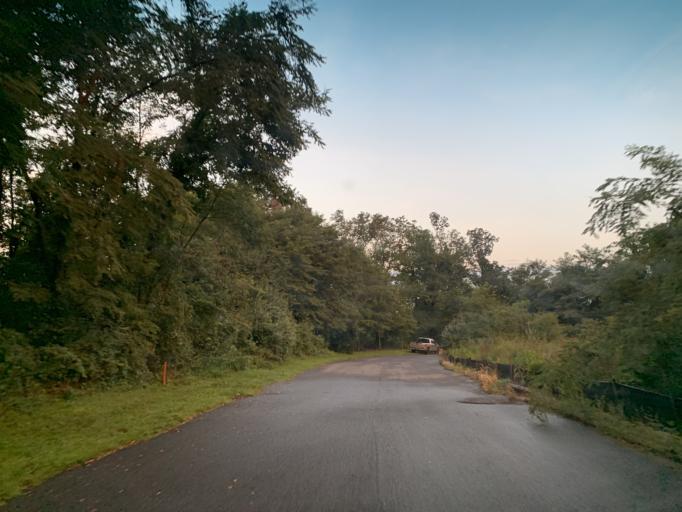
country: US
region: Maryland
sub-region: Harford County
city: Edgewood
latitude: 39.3947
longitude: -76.3451
